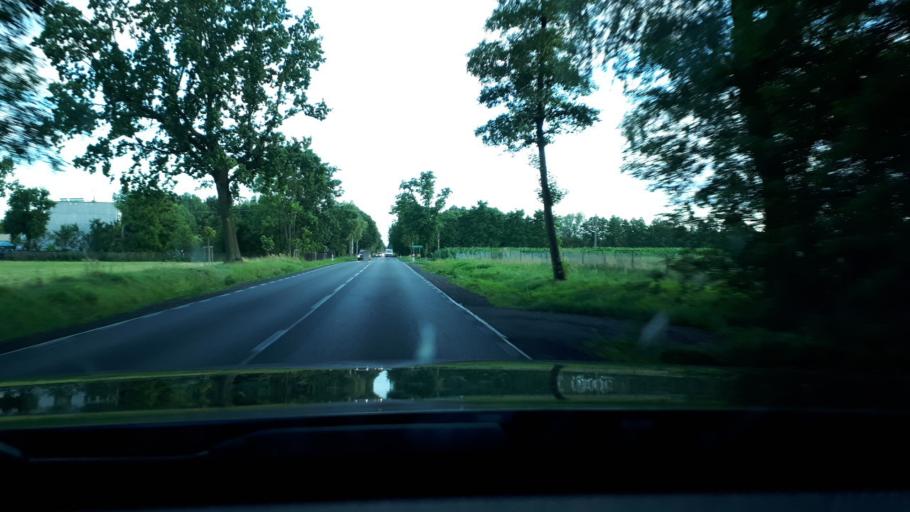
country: PL
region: Masovian Voivodeship
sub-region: Powiat ciechanowski
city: Ojrzen
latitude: 52.7546
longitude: 20.5356
